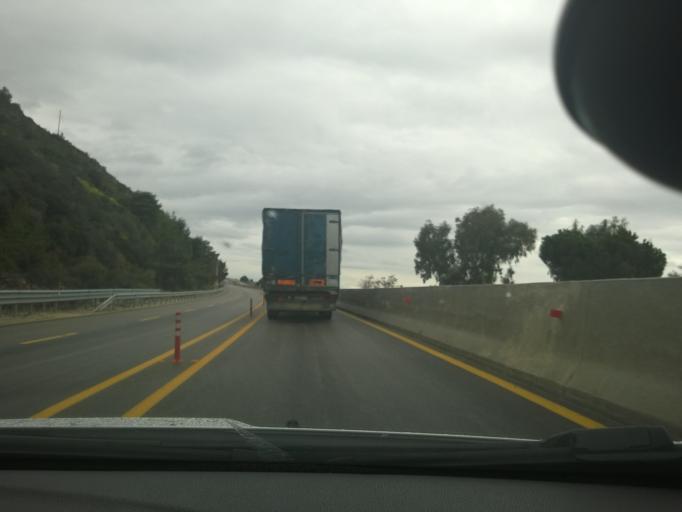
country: GR
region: West Greece
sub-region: Nomos Achaias
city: Siliveniotika
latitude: 38.1645
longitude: 22.3338
